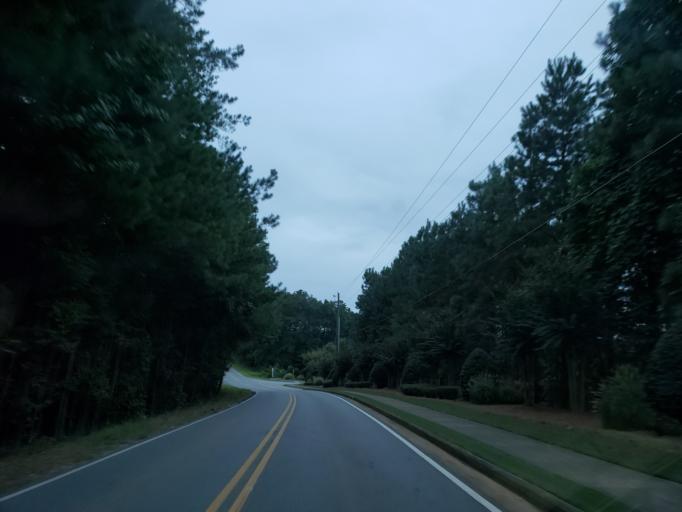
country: US
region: Georgia
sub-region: Cherokee County
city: Canton
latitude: 34.2866
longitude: -84.4538
